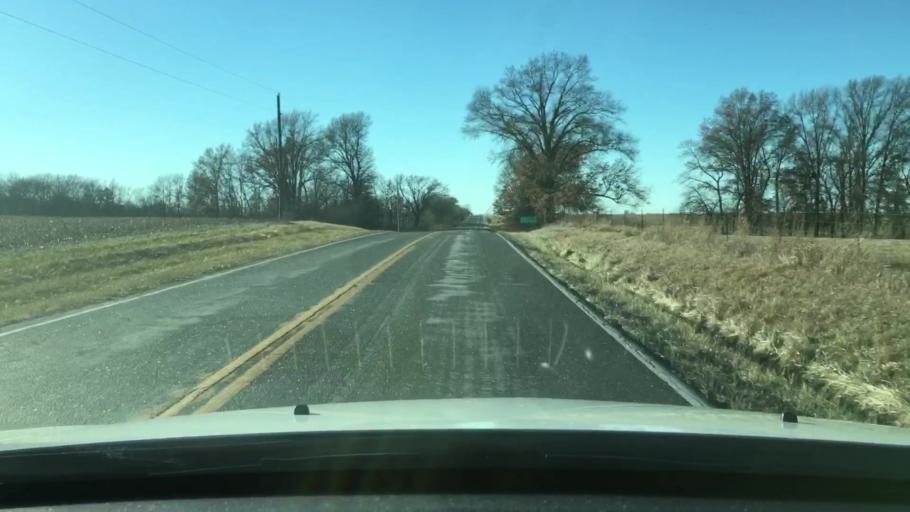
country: US
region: Missouri
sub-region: Audrain County
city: Mexico
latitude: 39.2817
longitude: -91.7177
